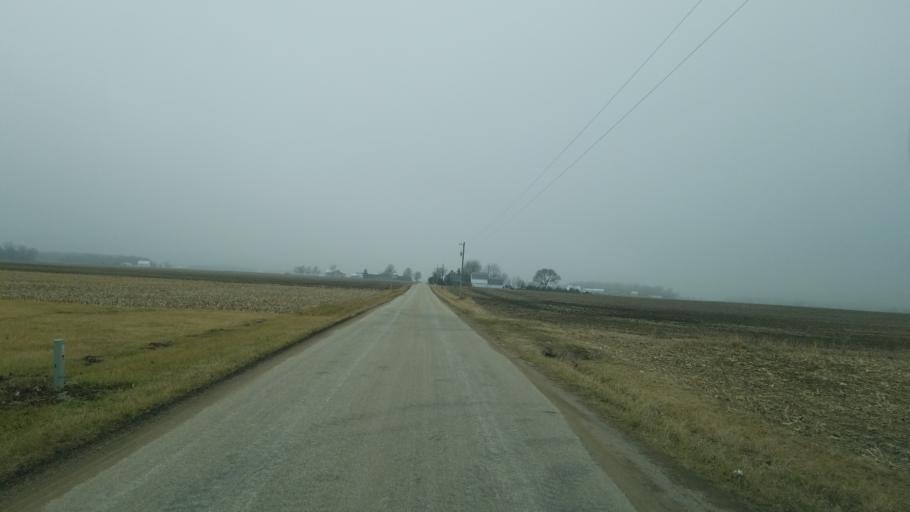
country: US
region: Indiana
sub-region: Adams County
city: Geneva
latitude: 40.5763
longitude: -85.0255
